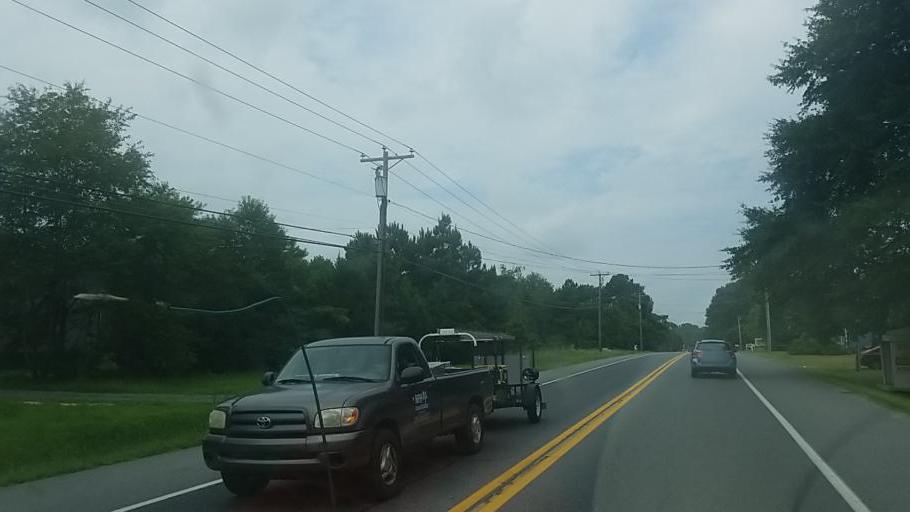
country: US
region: Delaware
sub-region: Sussex County
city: Ocean View
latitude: 38.5511
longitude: -75.1499
